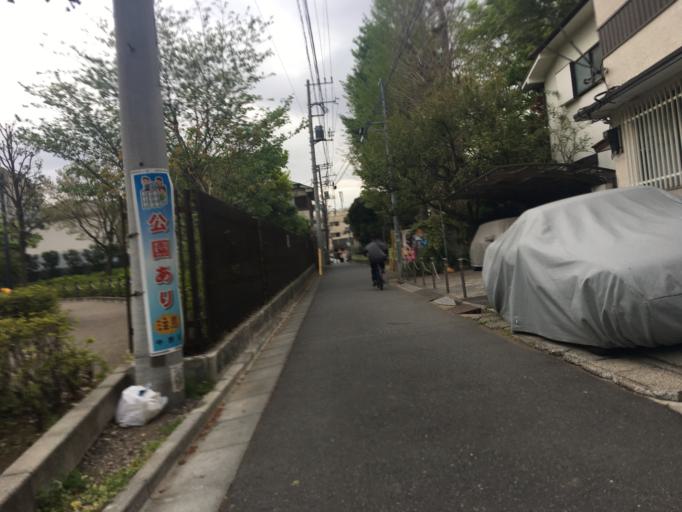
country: JP
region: Tokyo
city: Tokyo
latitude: 35.7067
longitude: 139.6581
